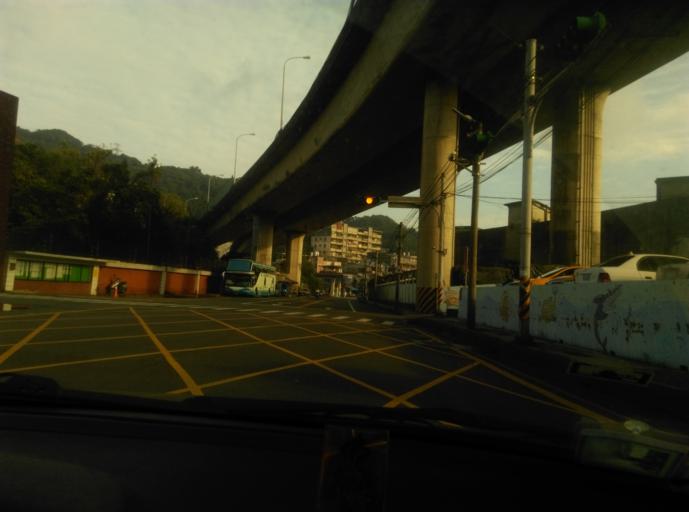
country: TW
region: Taiwan
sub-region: Keelung
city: Keelung
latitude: 25.1533
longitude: 121.7348
